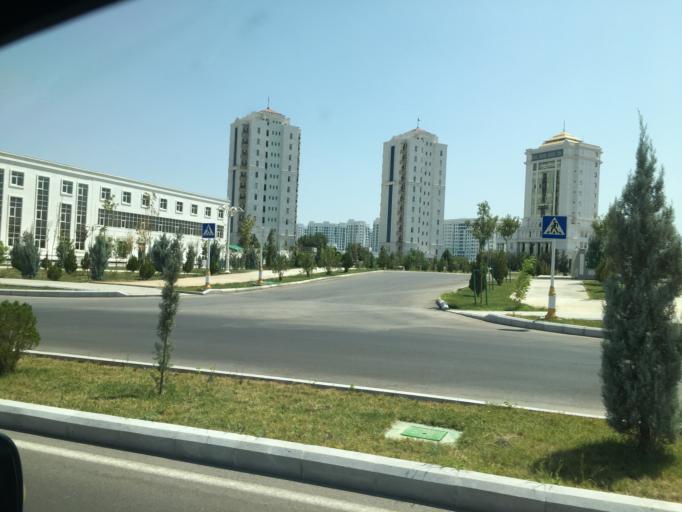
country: TM
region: Ahal
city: Ashgabat
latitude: 37.9154
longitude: 58.3671
